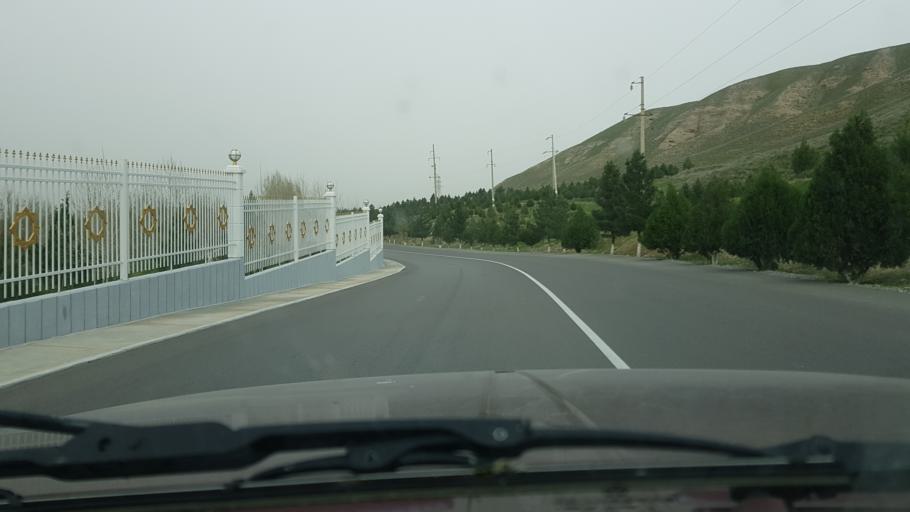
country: TM
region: Ahal
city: Arcabil
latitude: 38.0421
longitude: 58.0191
